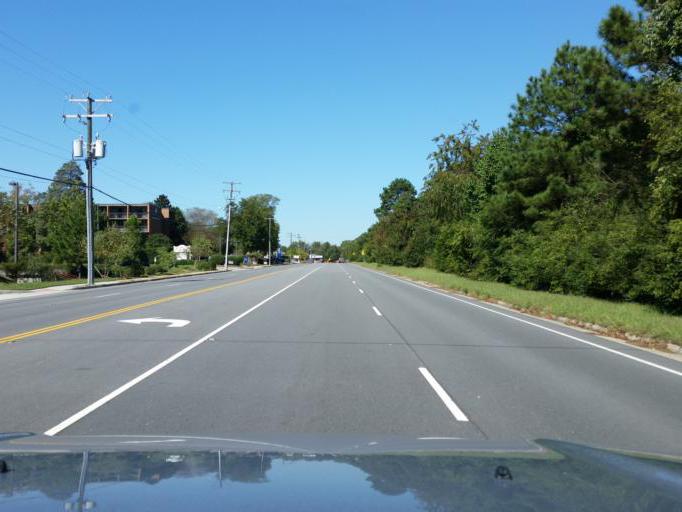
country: US
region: Virginia
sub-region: City of Williamsburg
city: Williamsburg
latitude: 37.2632
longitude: -76.6773
